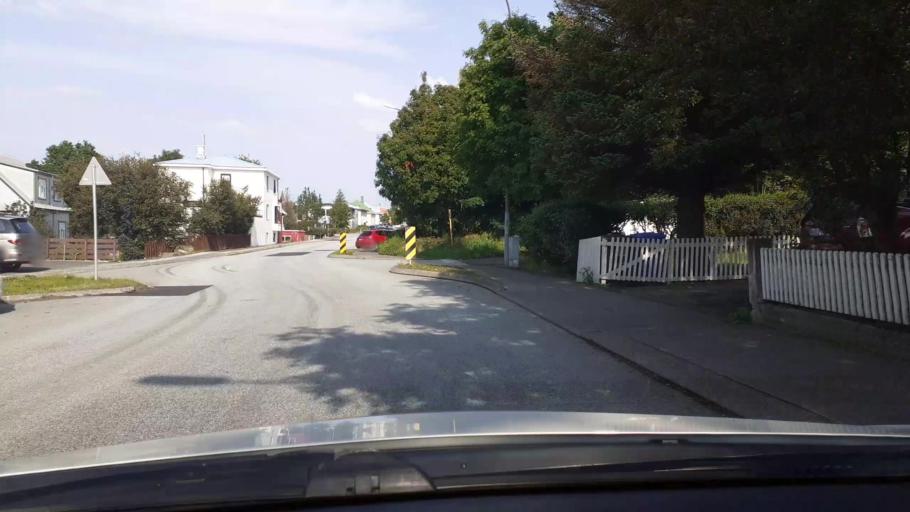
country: IS
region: Capital Region
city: Hafnarfjoerdur
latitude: 64.0621
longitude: -21.9560
